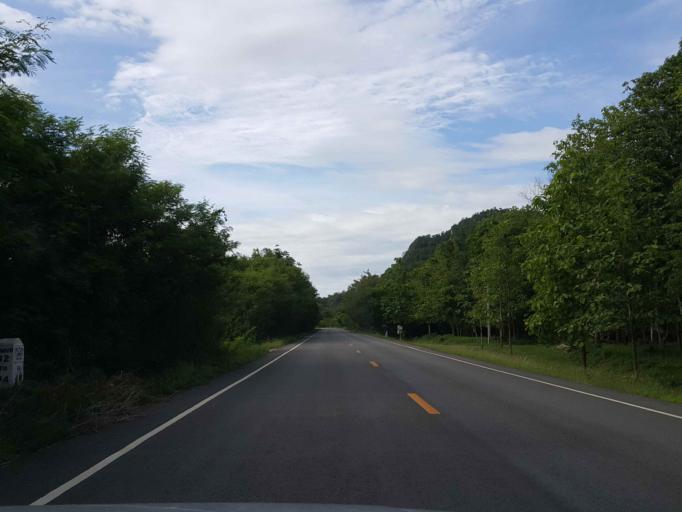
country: TH
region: Sukhothai
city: Thung Saliam
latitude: 17.2852
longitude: 99.5271
